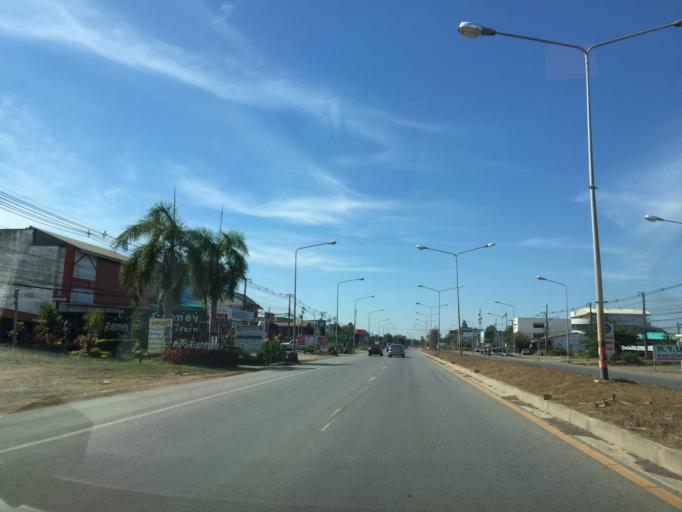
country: TH
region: Changwat Nong Bua Lamphu
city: Na Klang
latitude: 17.3033
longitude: 102.1988
